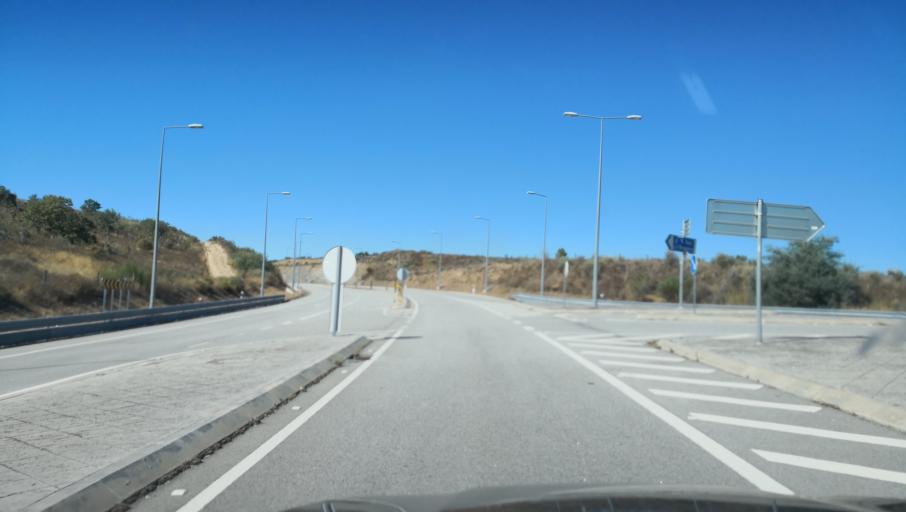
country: PT
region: Braganca
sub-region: Mirandela
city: Mirandela
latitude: 41.5164
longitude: -7.2277
